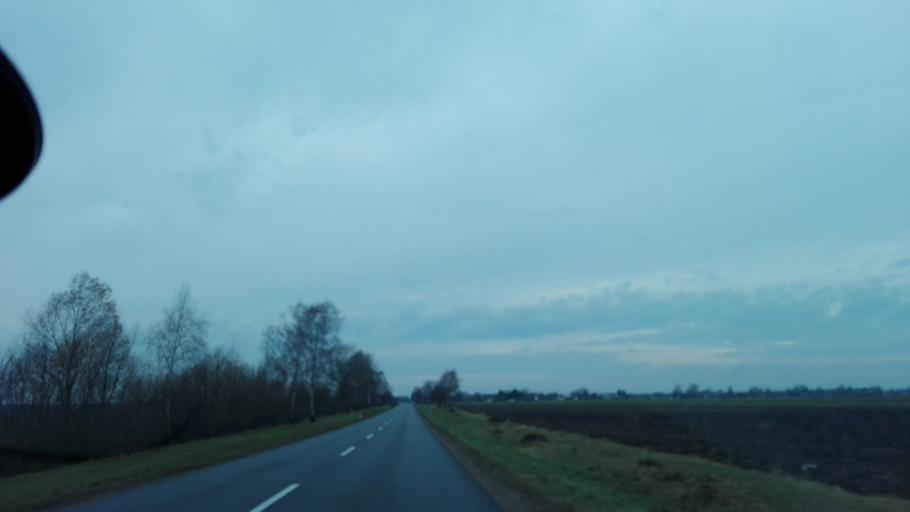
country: PL
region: Lublin Voivodeship
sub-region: Powiat radzynski
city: Komarowka Podlaska
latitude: 51.7761
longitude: 22.9367
